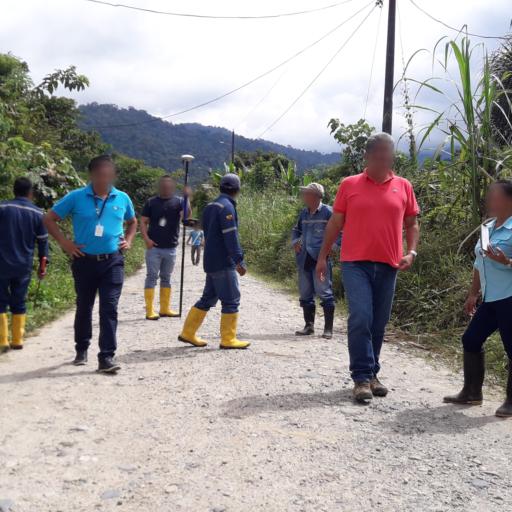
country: EC
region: Napo
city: Archidona
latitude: -0.9400
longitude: -77.8795
